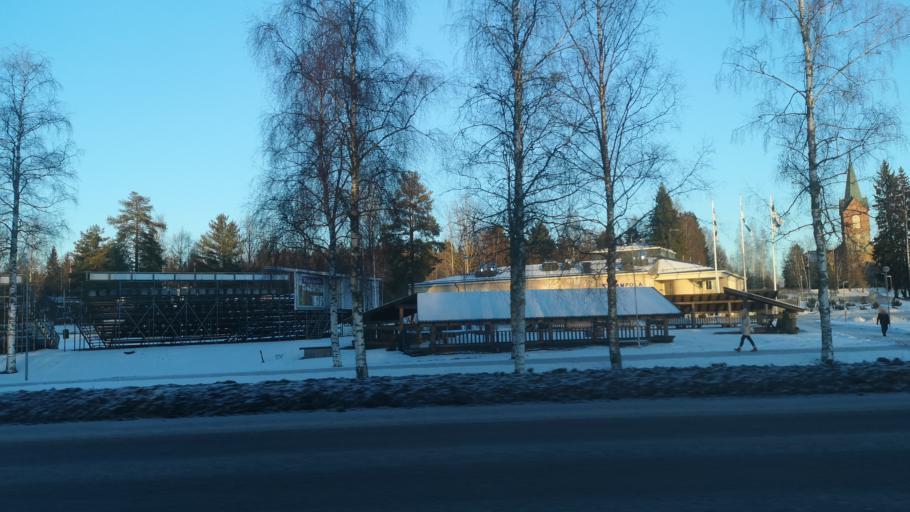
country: FI
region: Southern Savonia
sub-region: Pieksaemaeki
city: Juva
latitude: 61.8975
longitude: 27.8489
